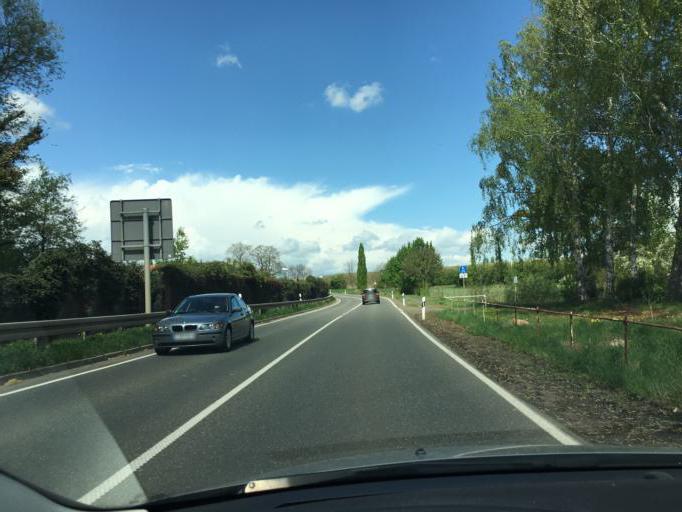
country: DE
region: Saxony
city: Frohburg
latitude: 51.0767
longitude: 12.5441
